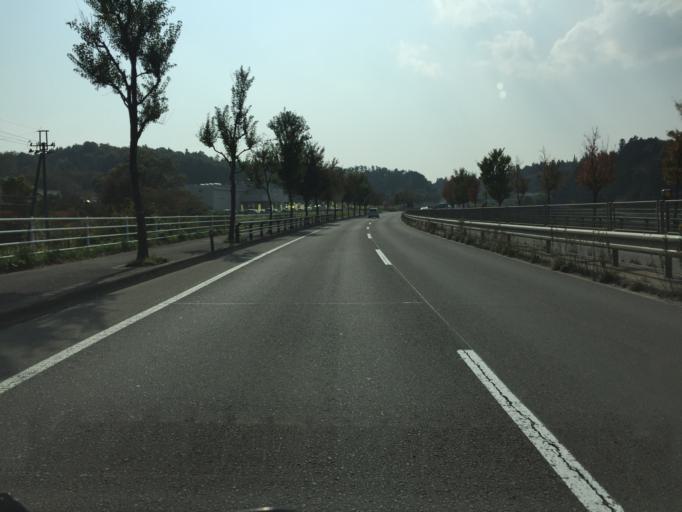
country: JP
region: Fukushima
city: Nihommatsu
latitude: 37.6259
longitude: 140.4803
